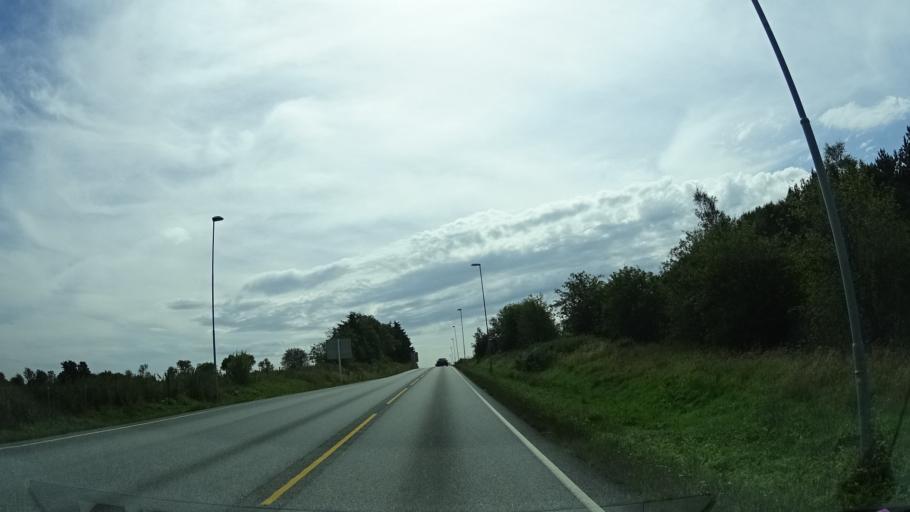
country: NO
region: Rogaland
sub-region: Randaberg
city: Randaberg
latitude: 59.0045
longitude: 5.6429
